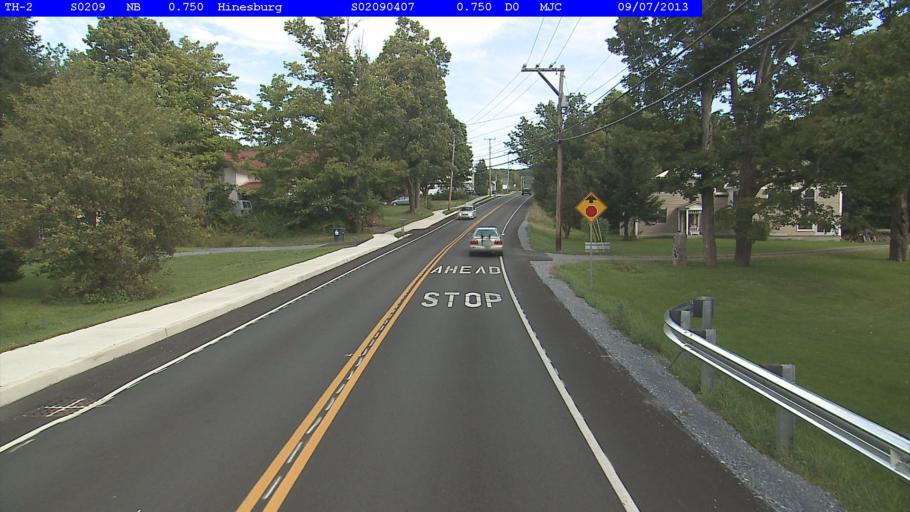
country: US
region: Vermont
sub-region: Chittenden County
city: Hinesburg
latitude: 44.3412
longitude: -73.1060
